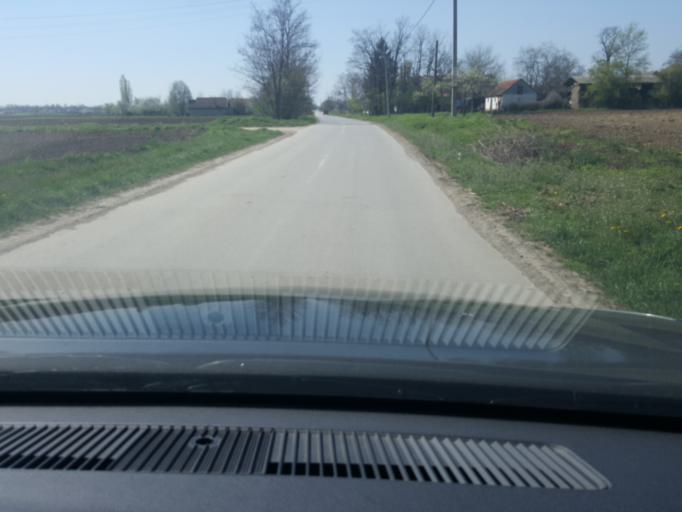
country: RS
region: Autonomna Pokrajina Vojvodina
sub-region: Zapadnobacki Okrug
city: Sombor
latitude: 45.7684
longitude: 19.0785
